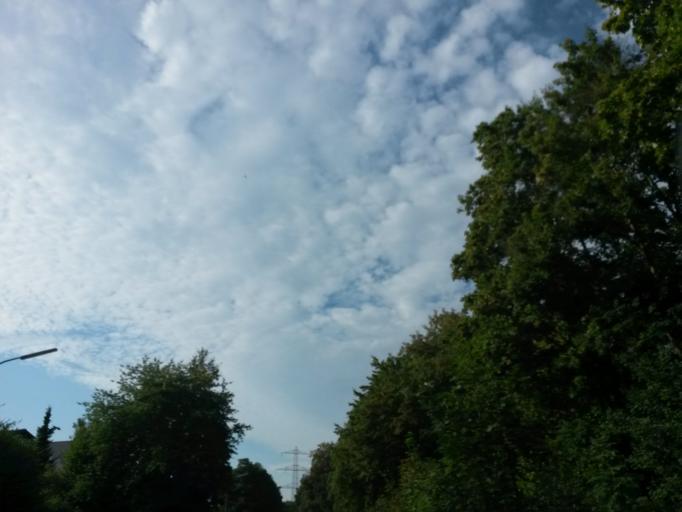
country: DE
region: North Rhine-Westphalia
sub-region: Regierungsbezirk Koln
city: Rosrath
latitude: 50.8825
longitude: 7.1915
